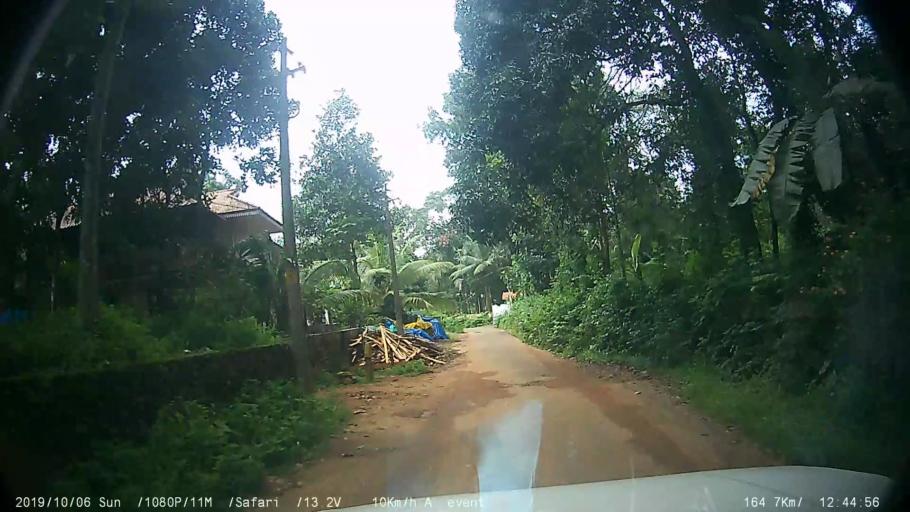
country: IN
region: Kerala
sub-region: Kottayam
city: Palackattumala
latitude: 9.7715
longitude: 76.6139
